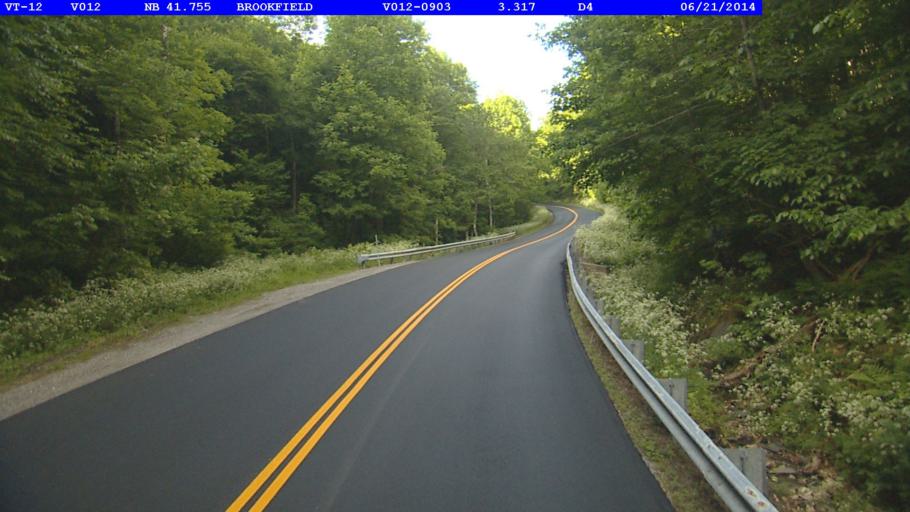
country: US
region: Vermont
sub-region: Washington County
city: Northfield
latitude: 44.0501
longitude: -72.6434
